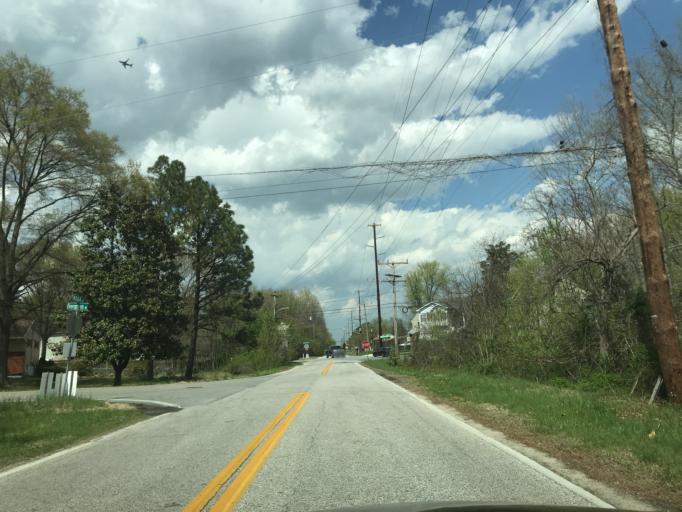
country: US
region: Maryland
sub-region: Anne Arundel County
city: Severn
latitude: 39.1137
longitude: -76.6837
